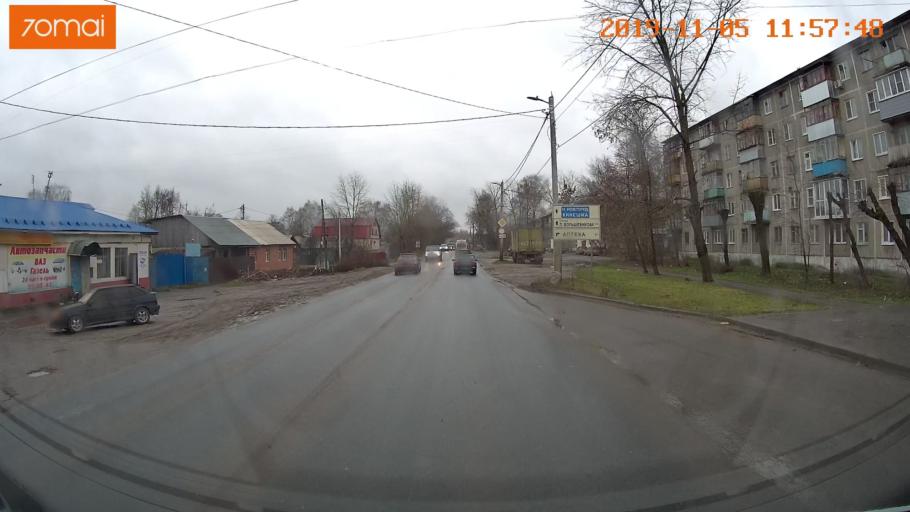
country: RU
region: Ivanovo
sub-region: Gorod Ivanovo
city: Ivanovo
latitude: 56.9823
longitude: 41.0366
